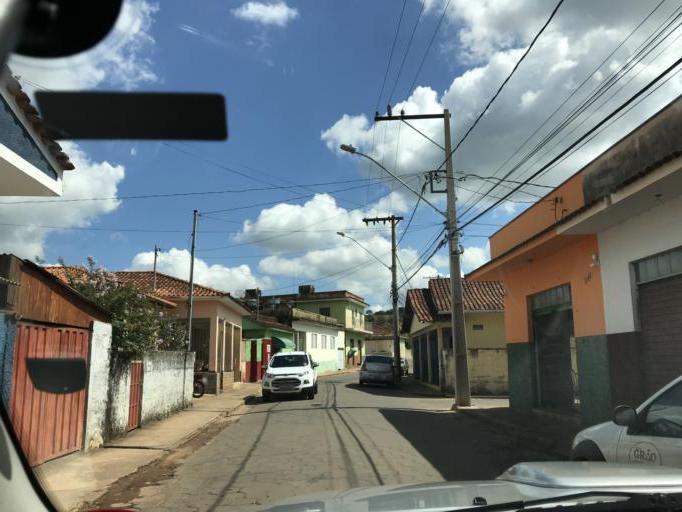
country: BR
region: Minas Gerais
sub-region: Campanha
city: Campanha
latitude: -21.8318
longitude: -45.4091
